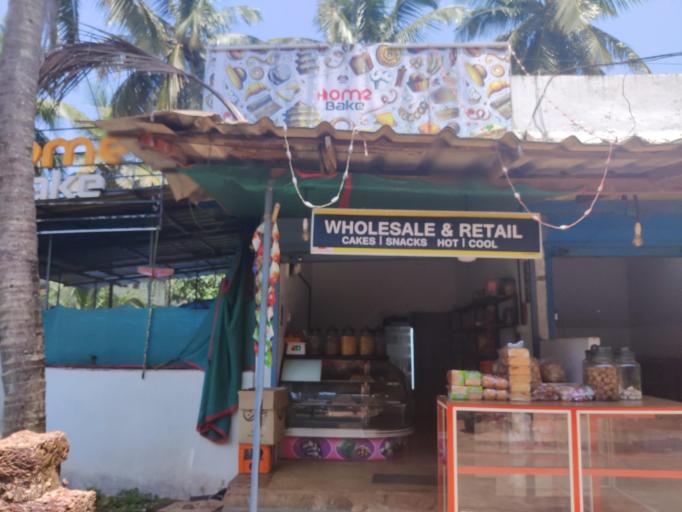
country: IN
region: Kerala
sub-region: Kasaragod District
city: Kannangad
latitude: 12.3984
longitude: 75.0485
